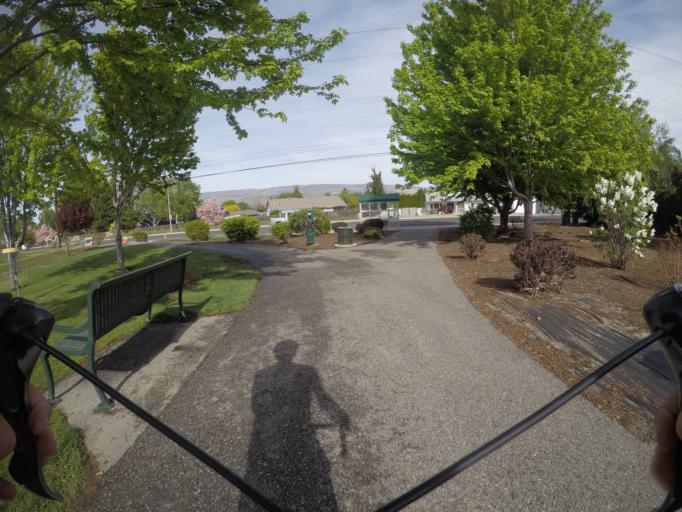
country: US
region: Washington
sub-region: Chelan County
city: West Wenatchee
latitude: 47.4432
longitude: -120.3468
